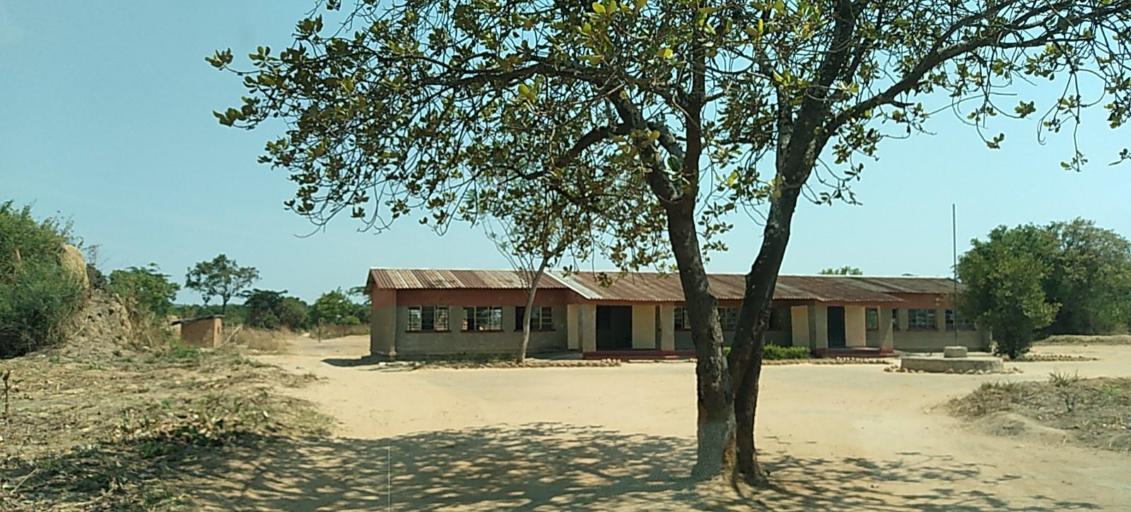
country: ZM
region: Copperbelt
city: Luanshya
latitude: -13.0062
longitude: 28.4770
